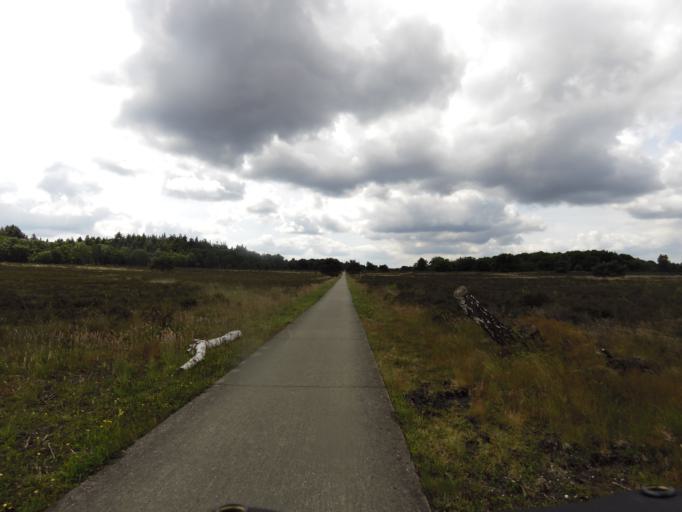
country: NL
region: Gelderland
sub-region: Gemeente Nunspeet
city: Nunspeet
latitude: 52.3185
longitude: 5.8144
